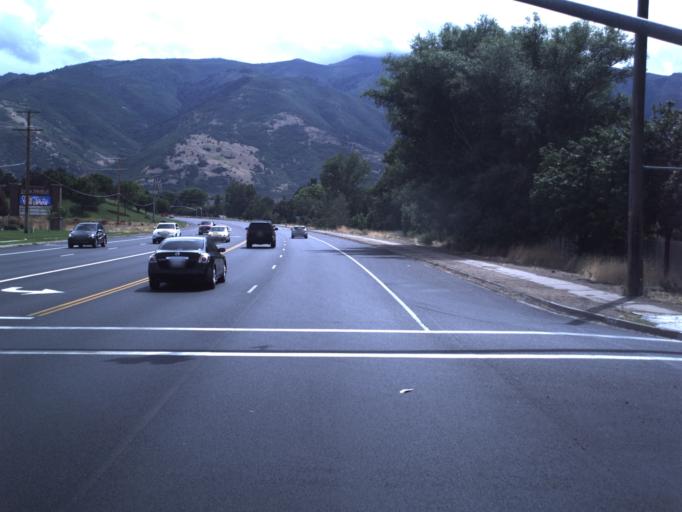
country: US
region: Utah
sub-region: Davis County
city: South Weber
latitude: 41.1012
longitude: -111.9392
